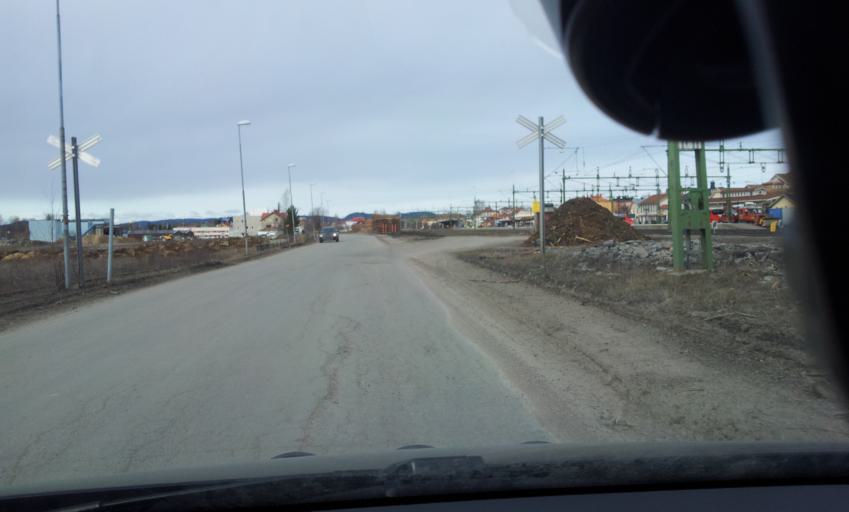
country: SE
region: Gaevleborg
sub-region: Ljusdals Kommun
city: Ljusdal
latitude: 61.8248
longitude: 16.1030
